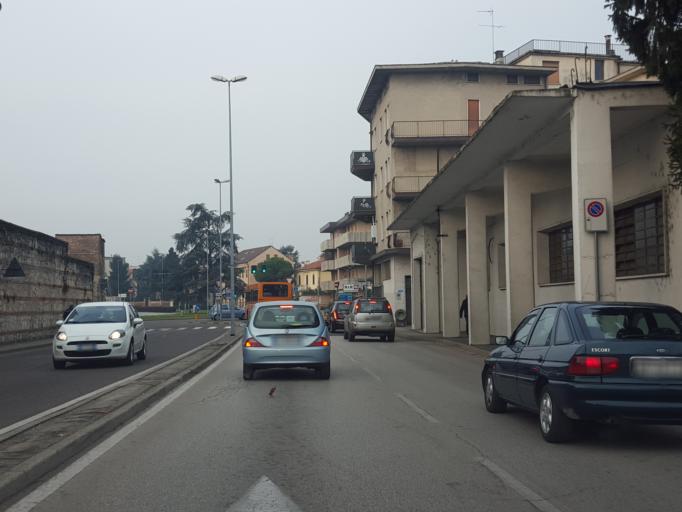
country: IT
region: Veneto
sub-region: Provincia di Vicenza
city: Vicenza
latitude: 45.5581
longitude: 11.5458
